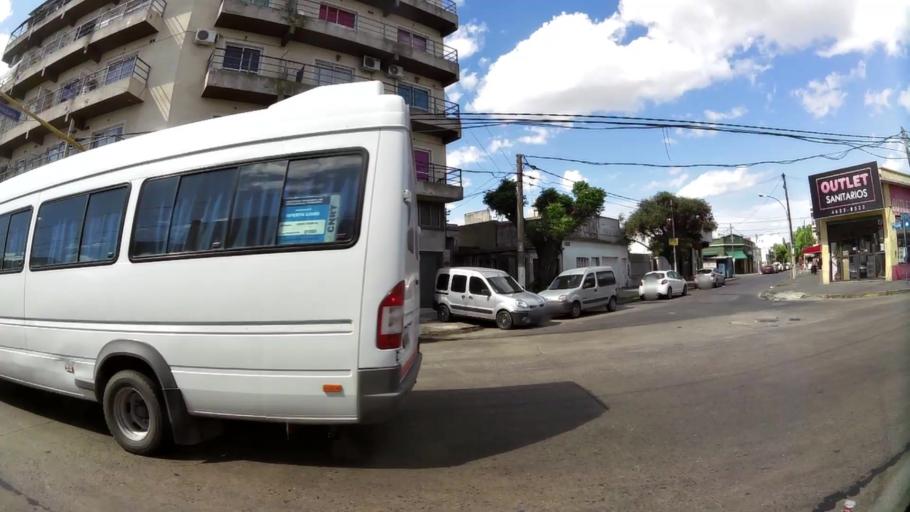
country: AR
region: Buenos Aires
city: San Justo
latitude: -34.6460
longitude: -58.5408
